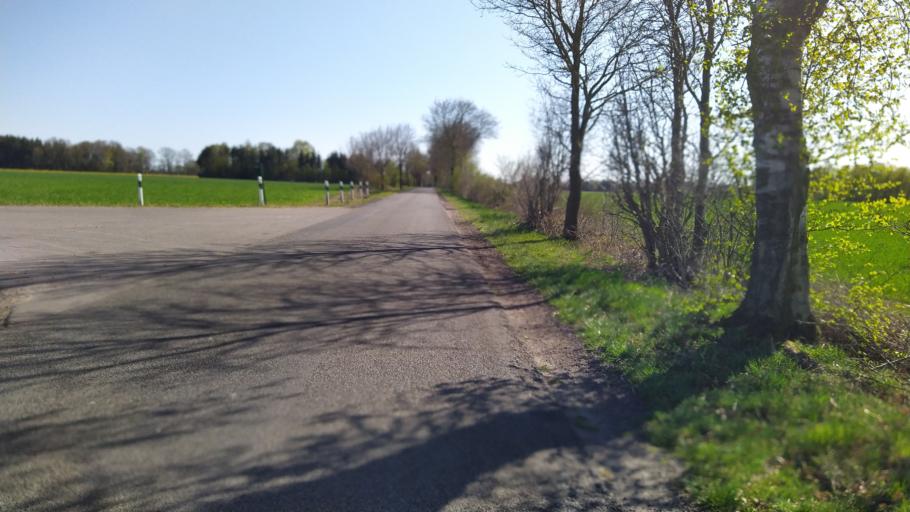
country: DE
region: Lower Saxony
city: Heeslingen
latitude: 53.3141
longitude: 9.3870
